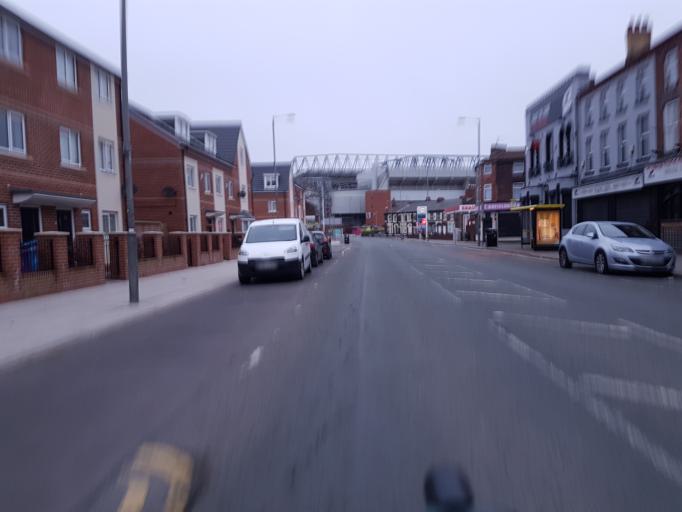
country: GB
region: England
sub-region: Liverpool
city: Liverpool
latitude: 53.4283
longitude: -2.9591
